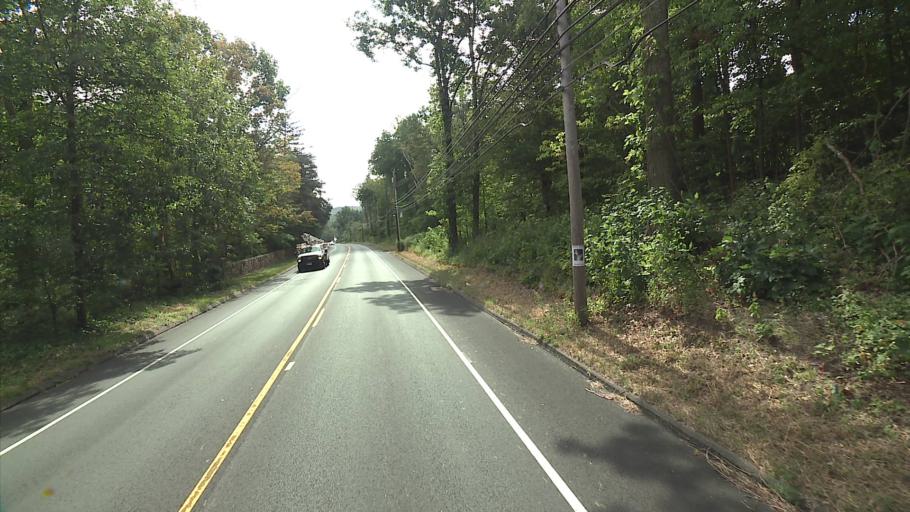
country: US
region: Connecticut
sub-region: Hartford County
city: Weatogue
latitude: 41.8347
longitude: -72.7790
